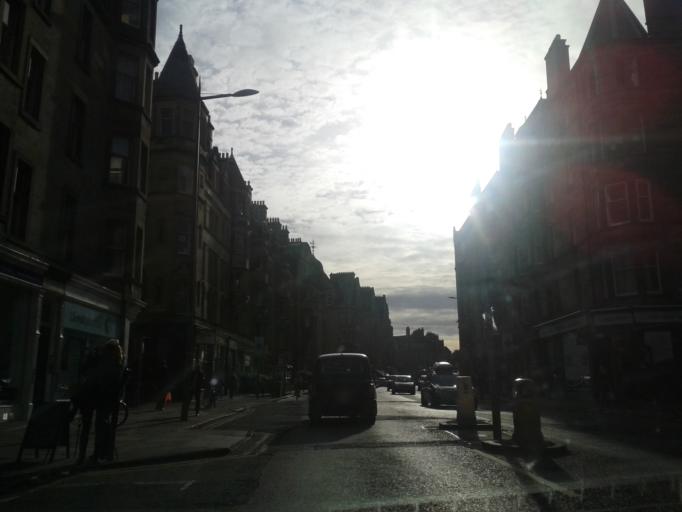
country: GB
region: Scotland
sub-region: Edinburgh
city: Edinburgh
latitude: 55.9370
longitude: -3.2073
